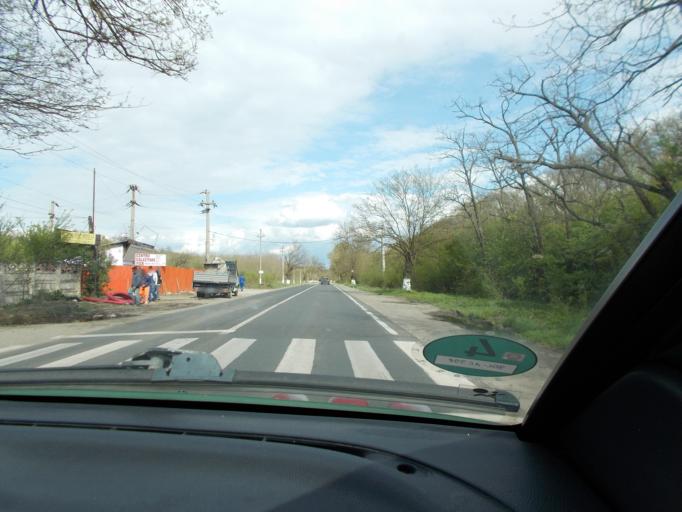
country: RO
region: Ilfov
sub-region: Comuna Ganeasa
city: Ganeasa
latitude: 44.4561
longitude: 26.2839
